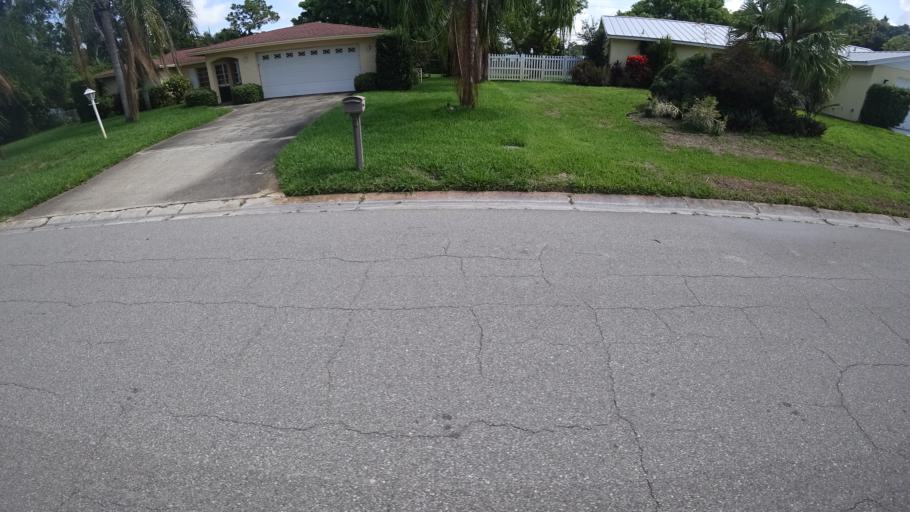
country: US
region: Florida
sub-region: Manatee County
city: Whitfield
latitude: 27.3950
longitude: -82.5665
